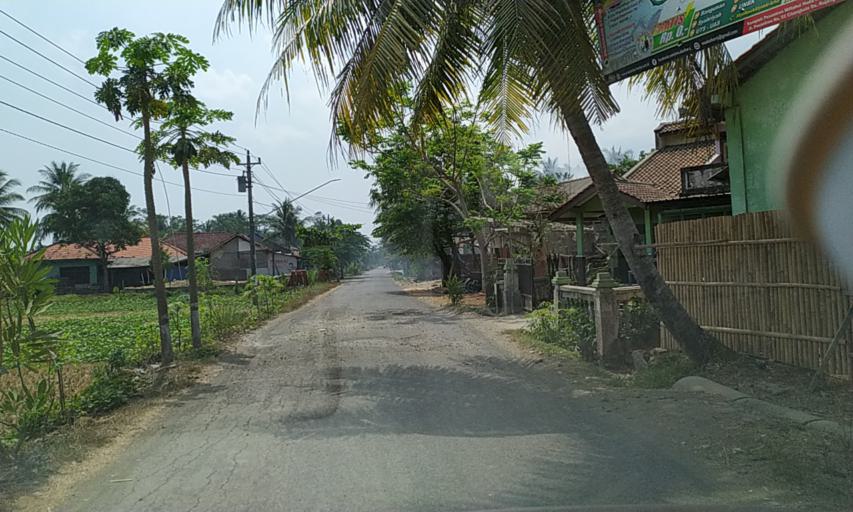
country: ID
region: Central Java
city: Karangtengah
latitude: -7.4459
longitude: 108.7534
